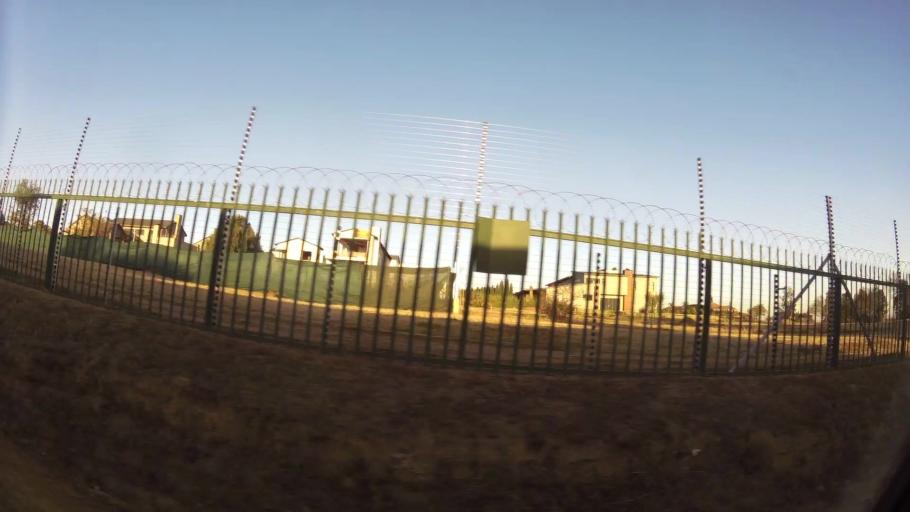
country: ZA
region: Gauteng
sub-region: City of Johannesburg Metropolitan Municipality
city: Diepsloot
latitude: -25.9422
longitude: 28.0401
